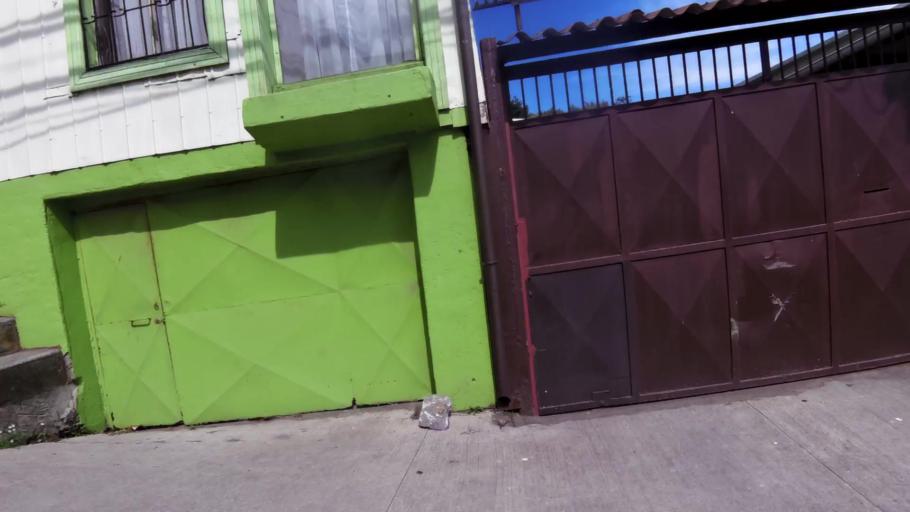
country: CL
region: Biobio
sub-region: Provincia de Concepcion
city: Talcahuano
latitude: -36.7159
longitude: -73.1112
